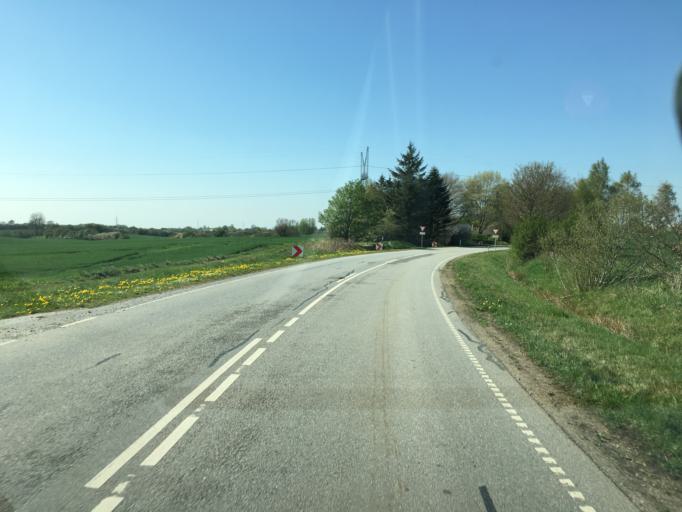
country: DK
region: South Denmark
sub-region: Haderslev Kommune
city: Vojens
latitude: 55.2932
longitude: 9.3861
